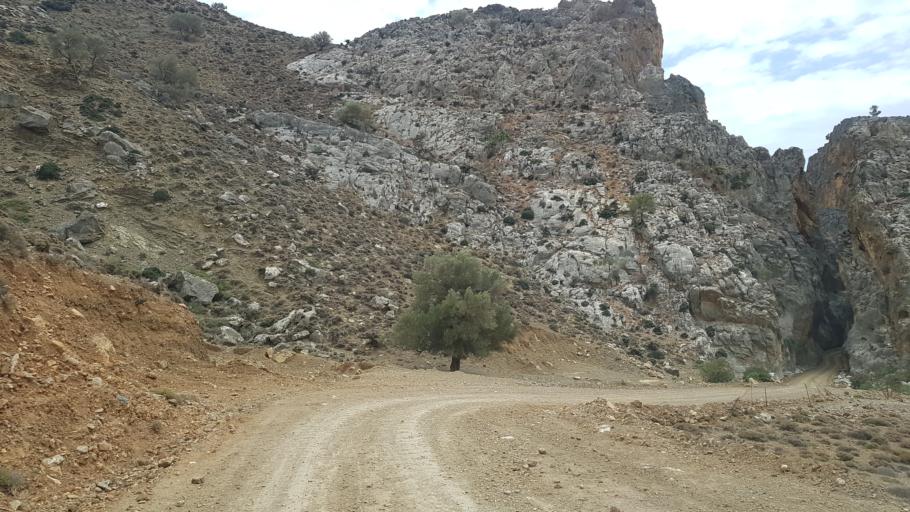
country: GR
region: Crete
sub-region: Nomos Irakleiou
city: Agioi Deka
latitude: 34.9440
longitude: 24.9856
